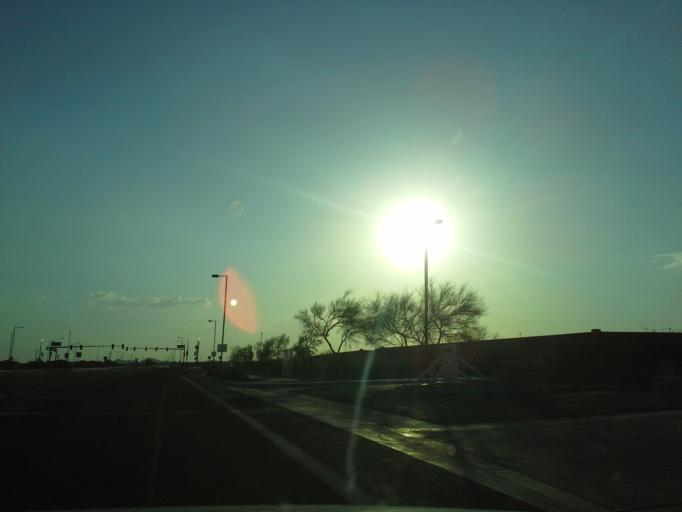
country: US
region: Arizona
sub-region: Maricopa County
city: Anthem
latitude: 33.7694
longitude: -112.1105
